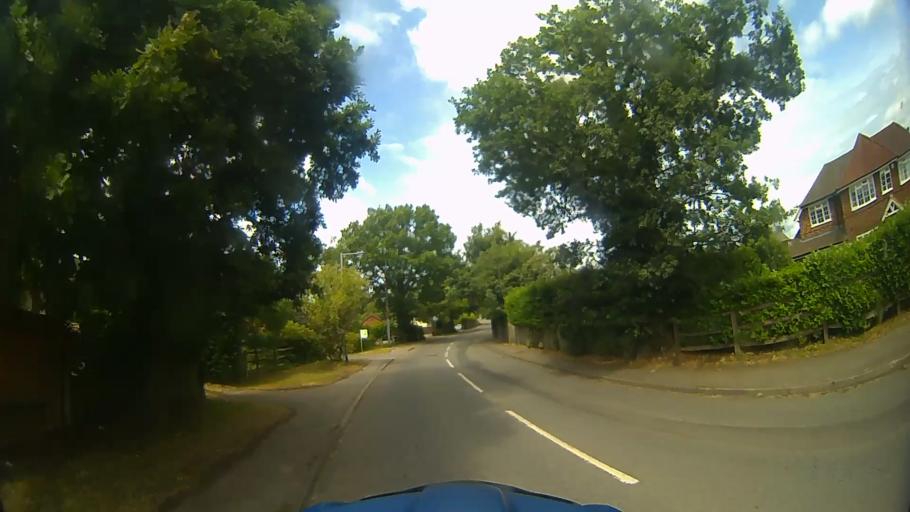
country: GB
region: England
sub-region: Wokingham
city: Barkham
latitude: 51.3996
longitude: -0.8760
